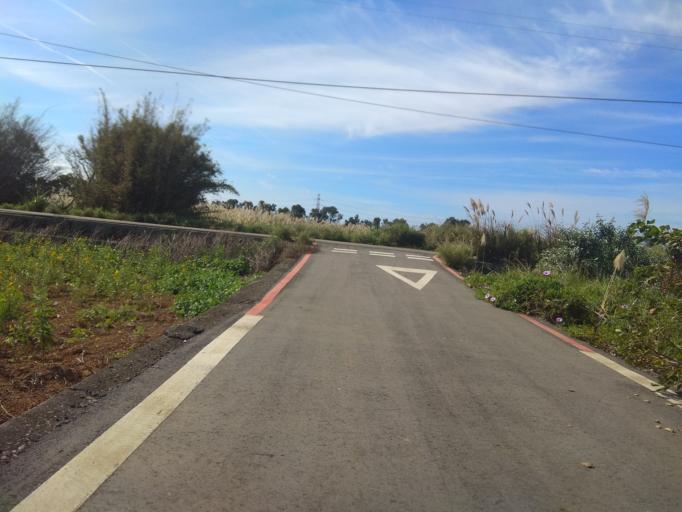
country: TW
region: Taiwan
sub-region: Hsinchu
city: Zhubei
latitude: 25.0201
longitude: 121.0627
